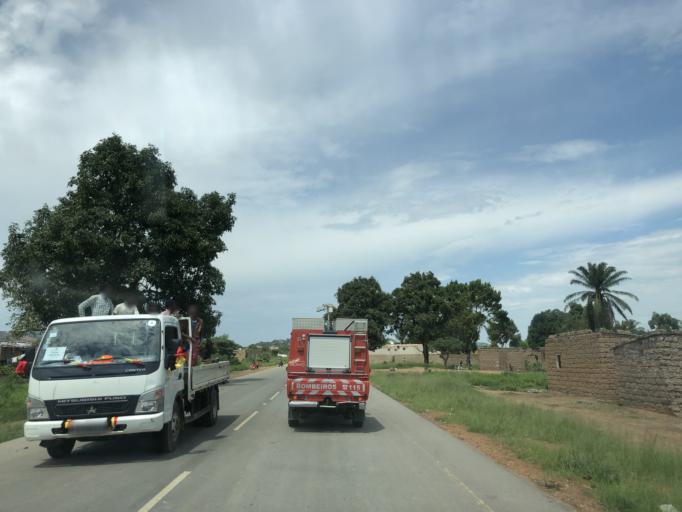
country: AO
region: Cuanza Sul
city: Quibala
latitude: -10.7356
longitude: 14.9955
